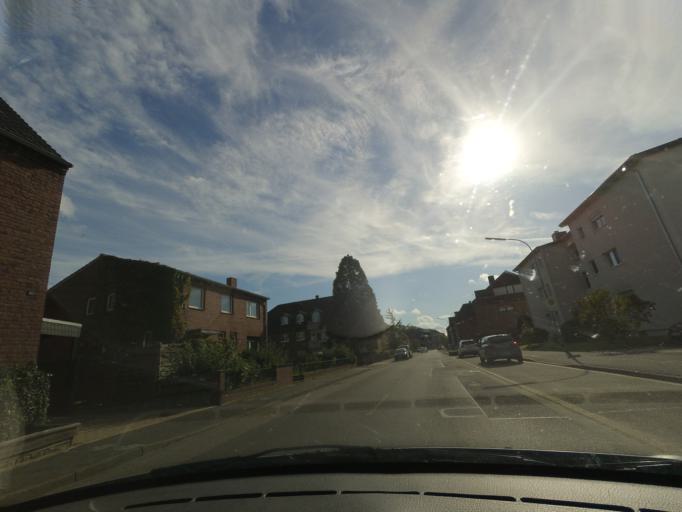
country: DE
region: North Rhine-Westphalia
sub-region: Regierungsbezirk Dusseldorf
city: Korschenbroich
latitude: 51.1914
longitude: 6.5564
